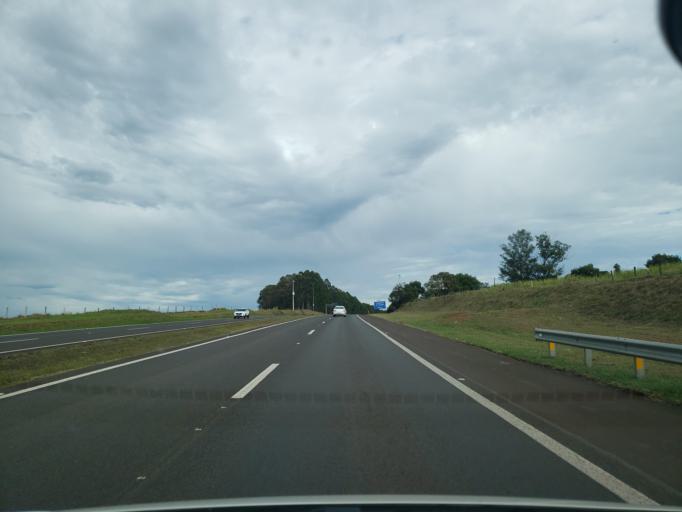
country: BR
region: Sao Paulo
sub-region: Dois Corregos
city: Dois Corregos
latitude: -22.2668
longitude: -48.3860
